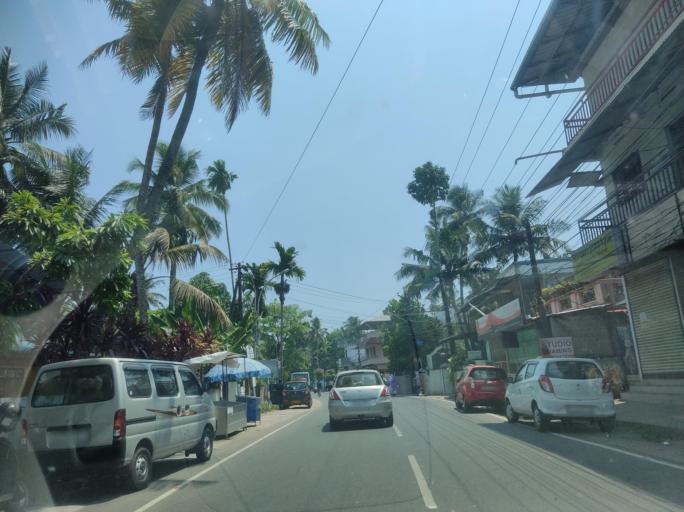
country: IN
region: Kerala
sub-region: Ernakulam
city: Cochin
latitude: 9.9070
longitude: 76.2804
